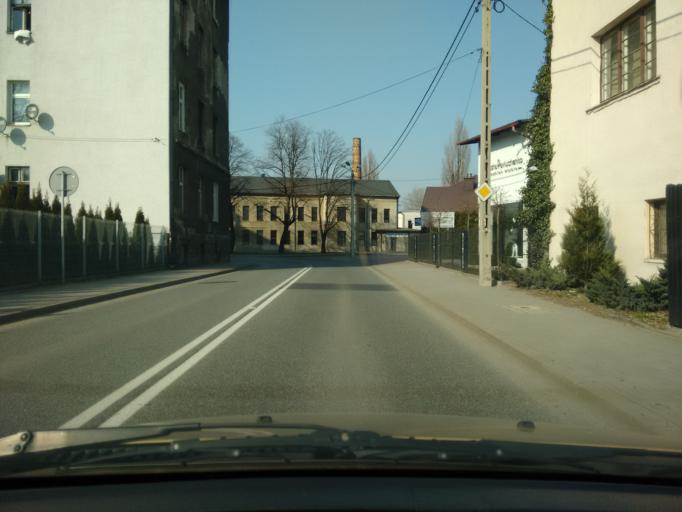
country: PL
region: Silesian Voivodeship
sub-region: Bielsko-Biala
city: Bielsko-Biala
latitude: 49.8361
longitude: 19.0493
